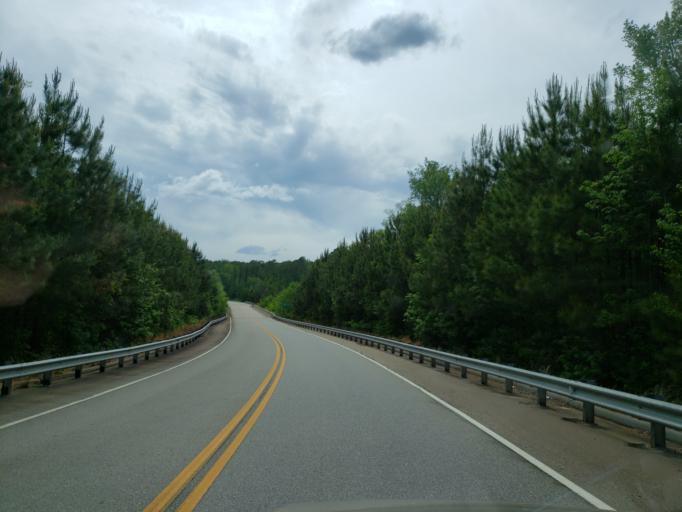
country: US
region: Georgia
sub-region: Monroe County
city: Forsyth
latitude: 32.9595
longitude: -83.9150
